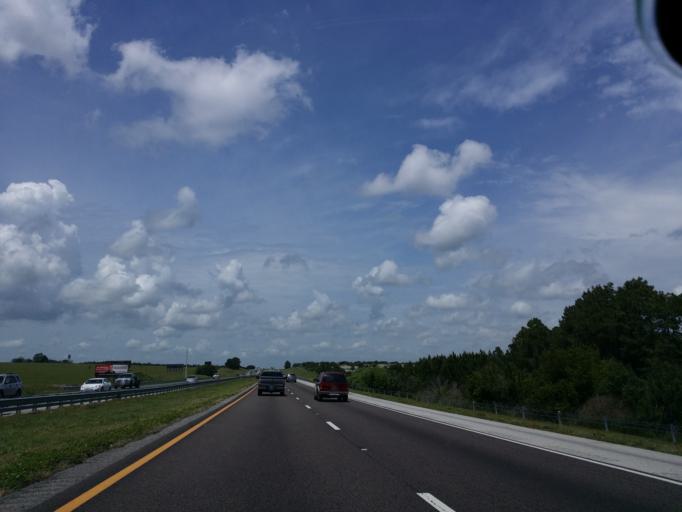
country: US
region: Florida
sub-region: Lake County
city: Hawthorne
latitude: 28.7057
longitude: -81.8863
